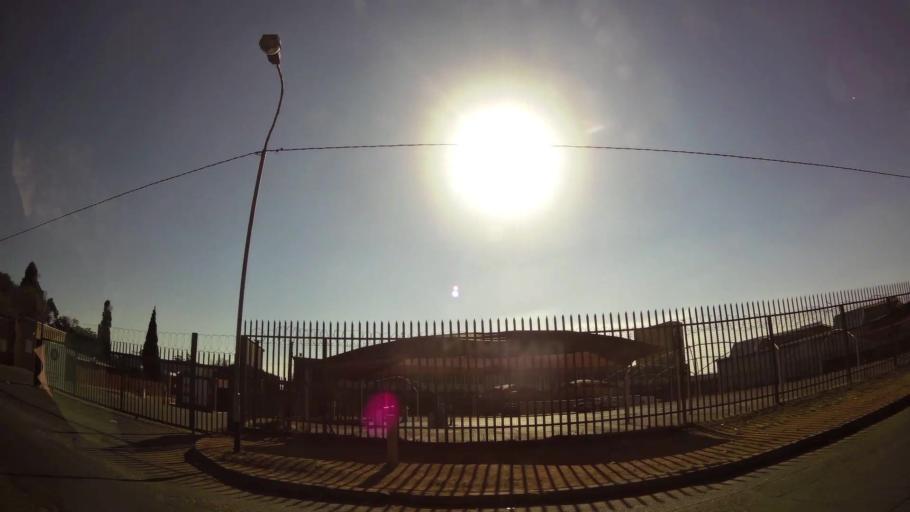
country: ZA
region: Gauteng
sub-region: City of Johannesburg Metropolitan Municipality
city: Johannesburg
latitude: -26.2079
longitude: 27.9803
